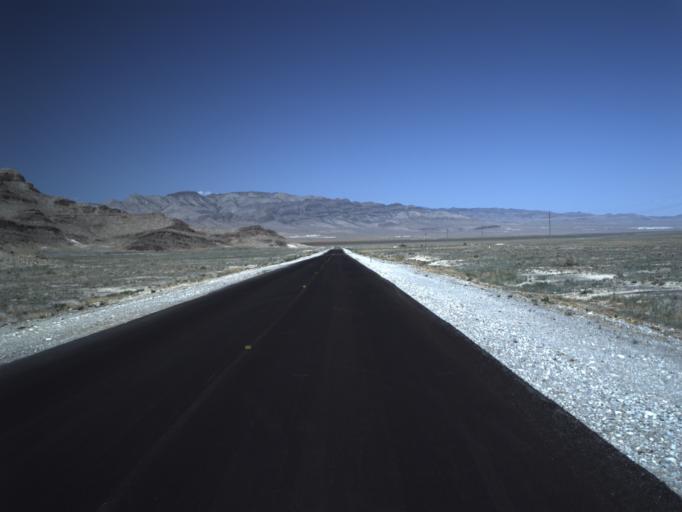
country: US
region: Utah
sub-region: Beaver County
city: Milford
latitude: 39.0554
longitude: -113.4285
